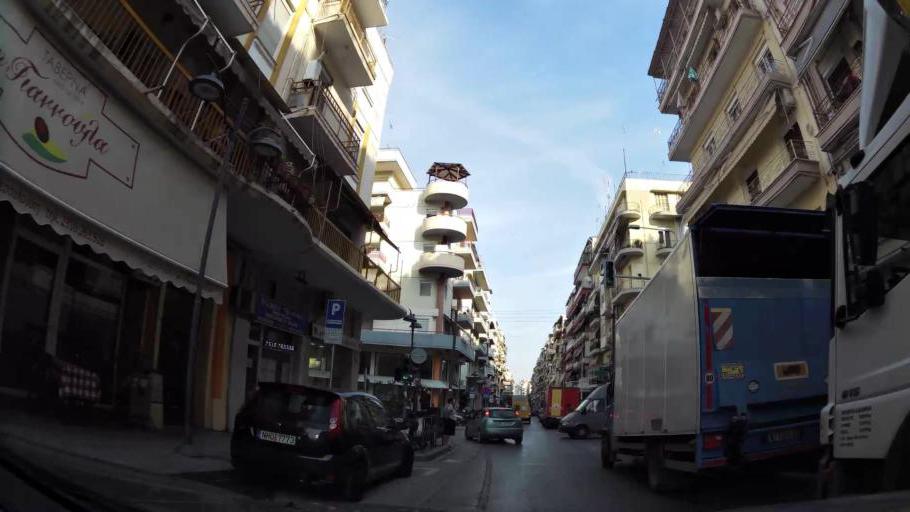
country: GR
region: Central Macedonia
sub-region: Nomos Thessalonikis
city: Sykies
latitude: 40.6401
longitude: 22.9470
